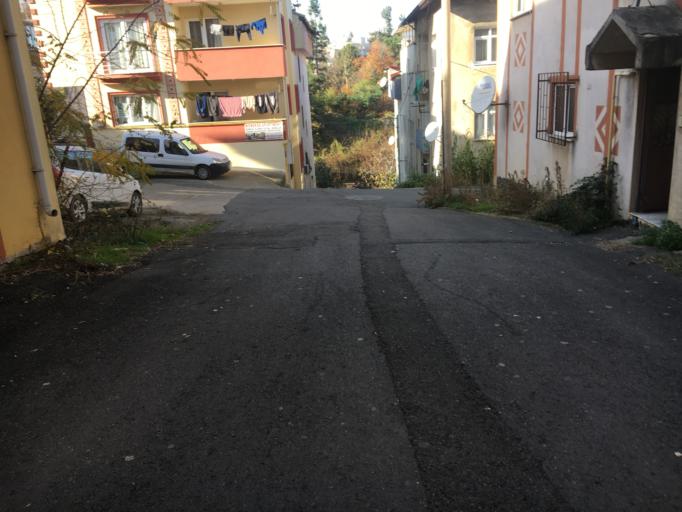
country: TR
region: Trabzon
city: Trabzon
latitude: 40.9928
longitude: 39.7787
